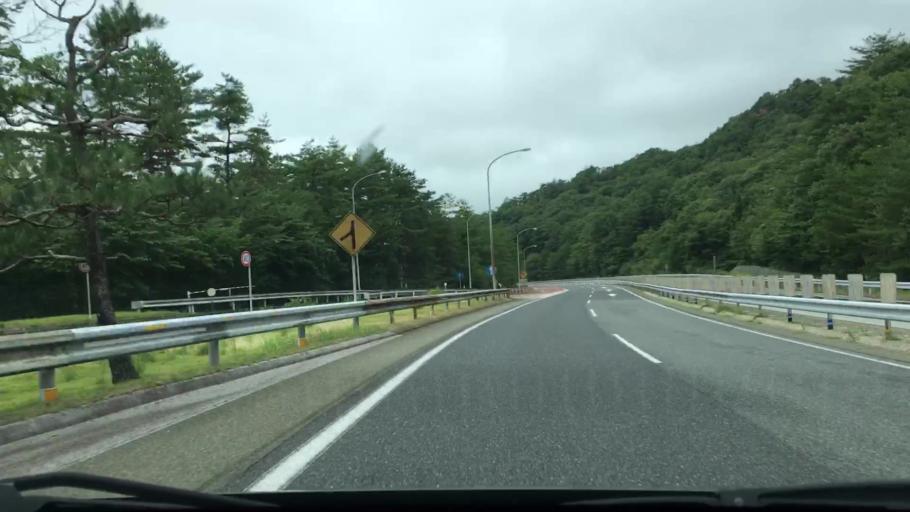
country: JP
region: Hiroshima
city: Shobara
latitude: 34.8619
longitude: 133.1037
